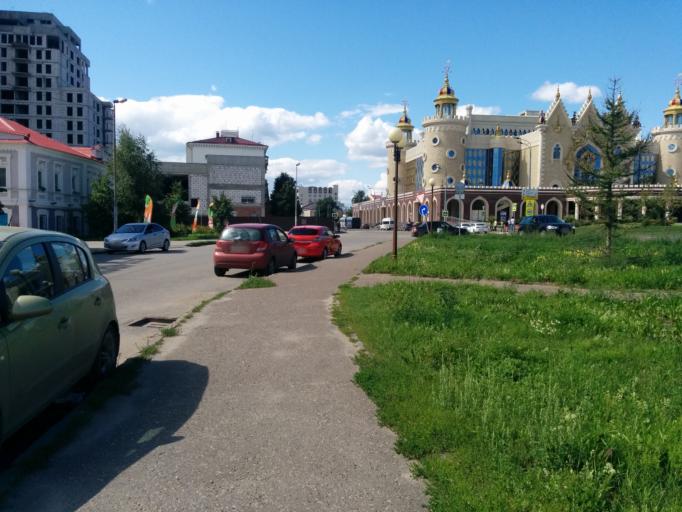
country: RU
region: Tatarstan
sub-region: Gorod Kazan'
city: Kazan
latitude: 55.7784
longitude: 49.1392
